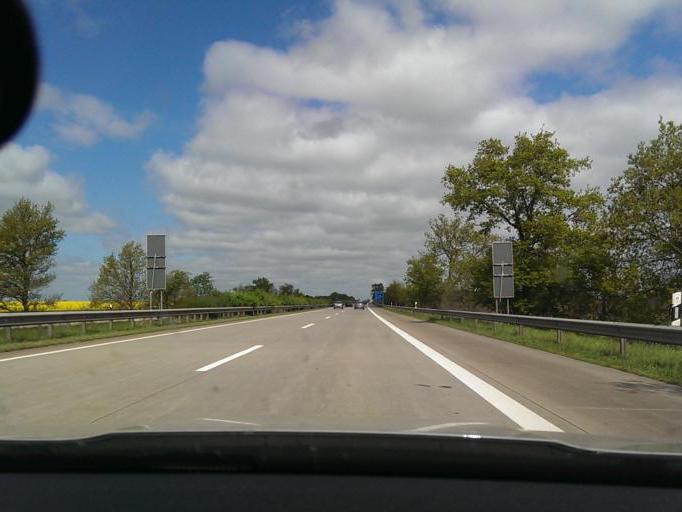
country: DE
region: Lower Saxony
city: Verden
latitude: 52.9494
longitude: 9.2556
